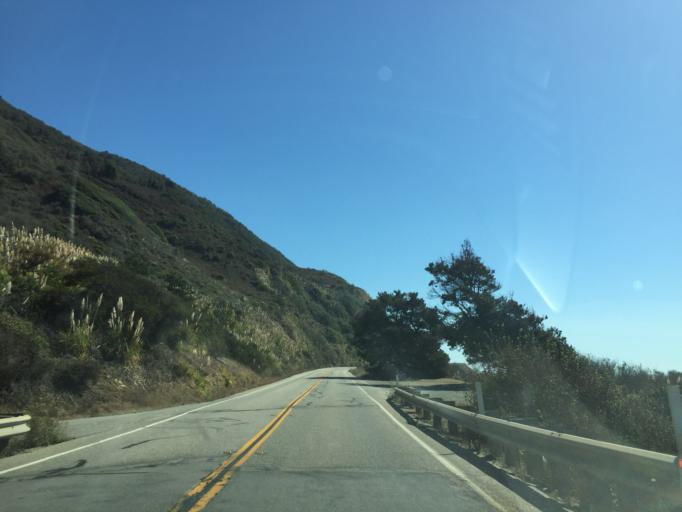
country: US
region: California
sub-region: Monterey County
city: Greenfield
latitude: 35.9830
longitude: -121.4909
